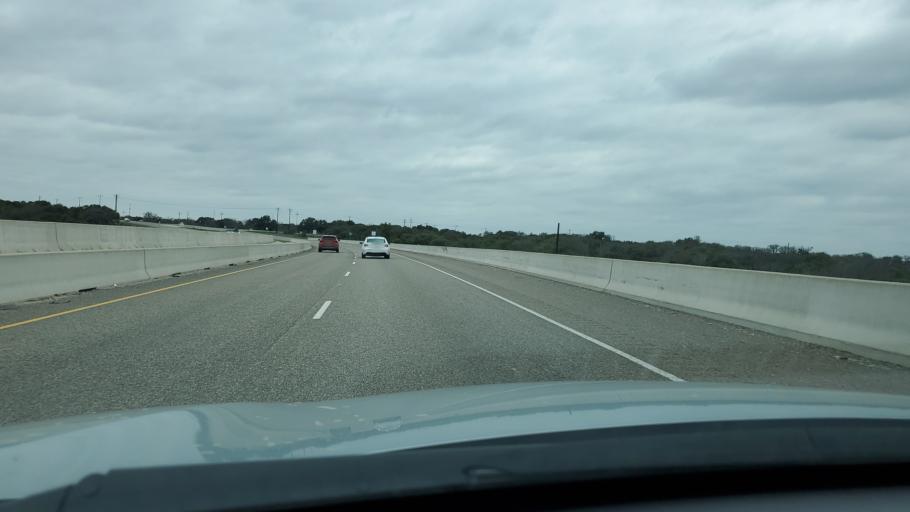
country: US
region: Texas
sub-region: Williamson County
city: Serenada
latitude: 30.7572
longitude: -97.7206
